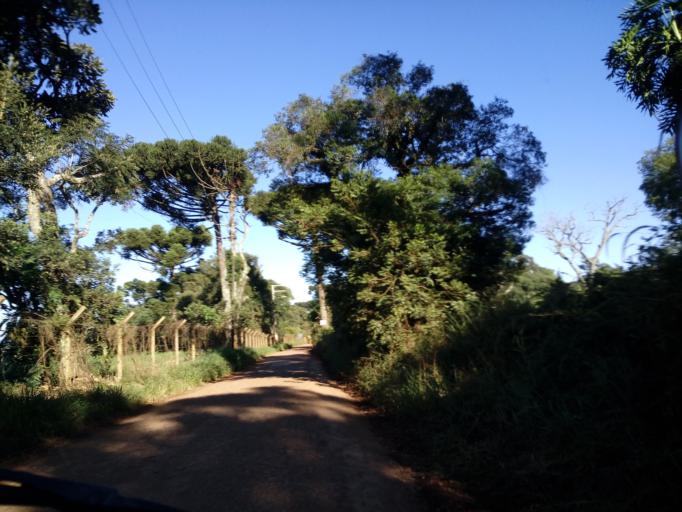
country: BR
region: Santa Catarina
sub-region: Chapeco
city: Chapeco
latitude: -27.1924
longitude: -52.6601
